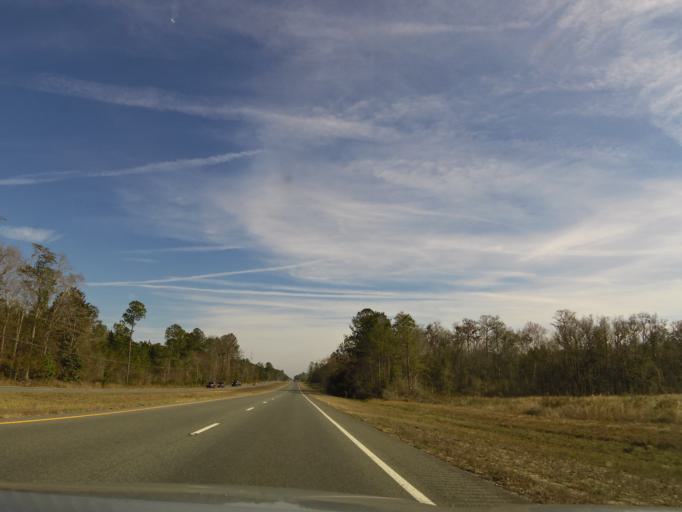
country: US
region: Georgia
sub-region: Brantley County
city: Nahunta
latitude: 31.2275
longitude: -81.8081
